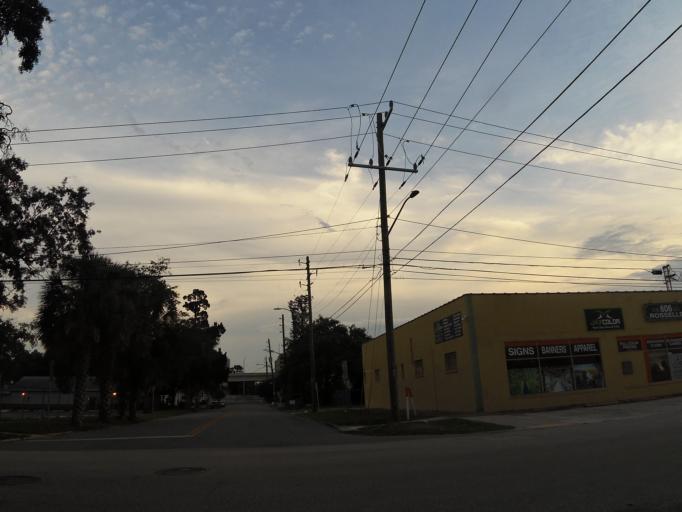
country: US
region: Florida
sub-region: Duval County
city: Jacksonville
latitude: 30.3195
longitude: -81.6775
